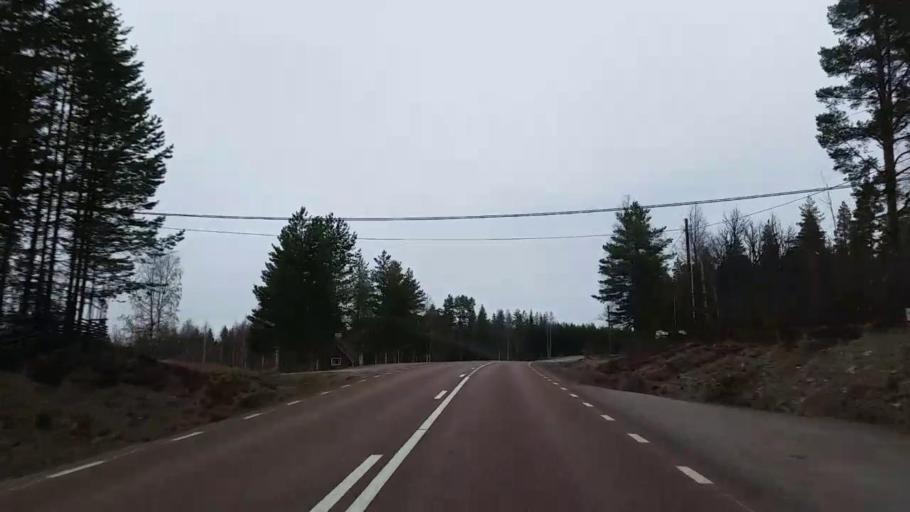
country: SE
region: Gaevleborg
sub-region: Ovanakers Kommun
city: Edsbyn
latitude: 61.2243
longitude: 15.8764
